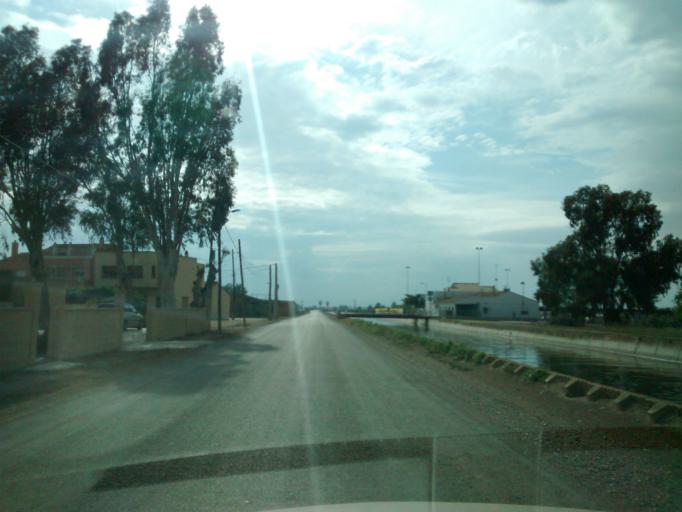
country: ES
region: Catalonia
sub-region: Provincia de Tarragona
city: Deltebre
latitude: 40.7024
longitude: 0.7354
